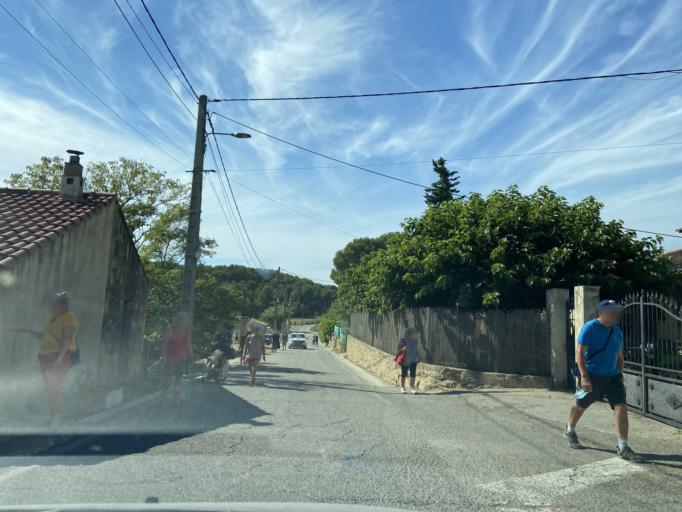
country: FR
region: Provence-Alpes-Cote d'Azur
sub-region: Departement des Bouches-du-Rhone
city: Saint-Chamas
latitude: 43.5637
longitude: 5.0229
